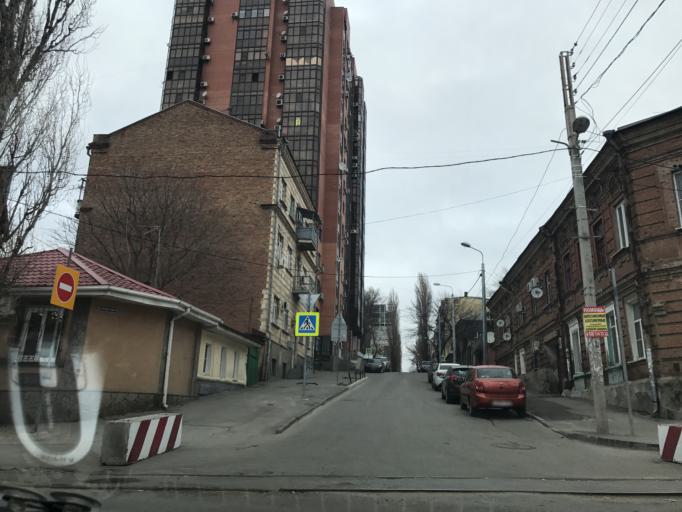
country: RU
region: Rostov
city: Rostov-na-Donu
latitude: 47.2229
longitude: 39.7379
